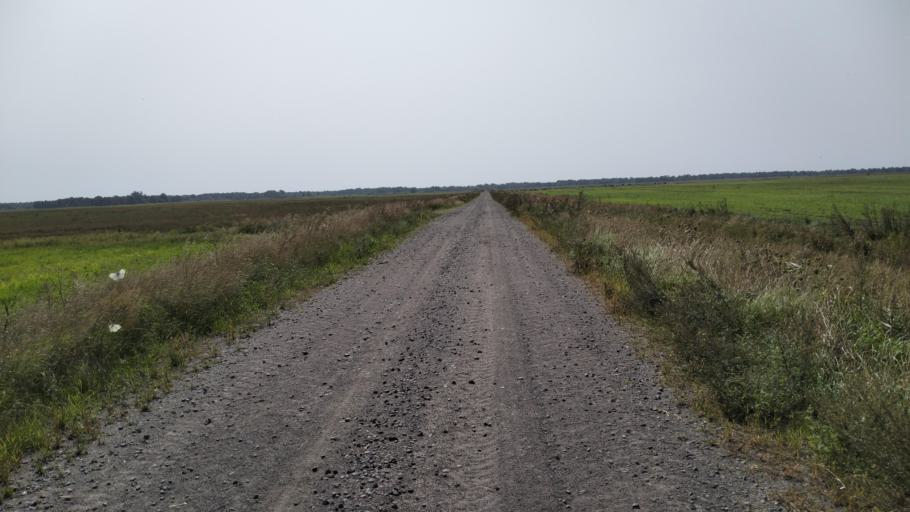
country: BY
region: Brest
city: Davyd-Haradok
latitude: 51.9866
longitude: 27.1755
